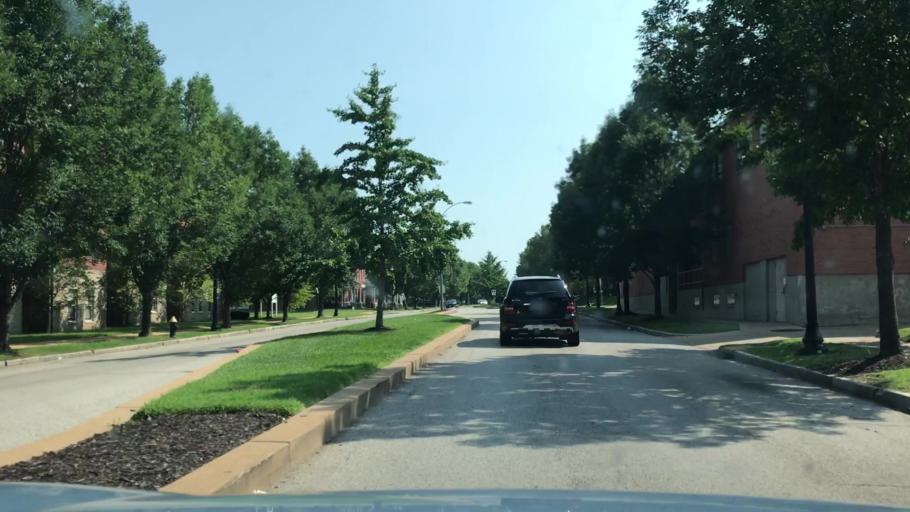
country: US
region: Missouri
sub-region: City of Saint Louis
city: St. Louis
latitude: 38.6190
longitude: -90.2047
